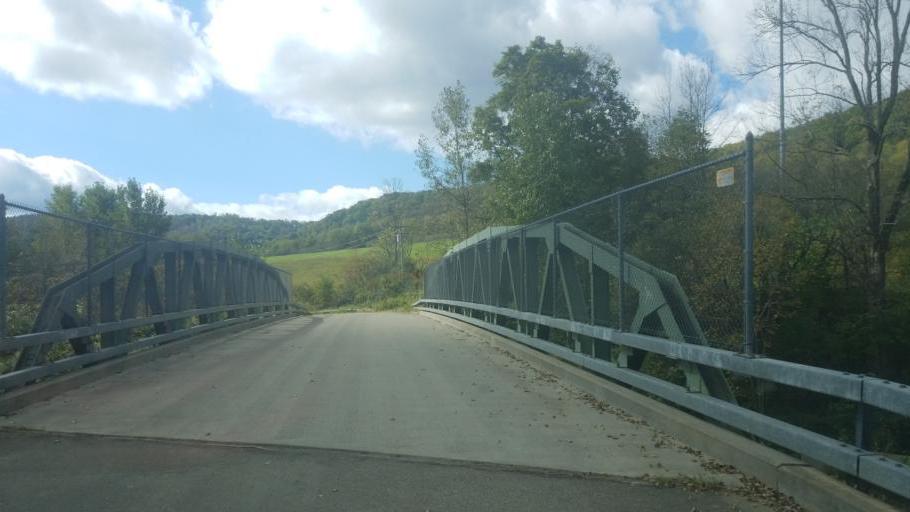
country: US
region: New York
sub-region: Cattaraugus County
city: Franklinville
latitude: 42.2420
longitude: -78.3985
